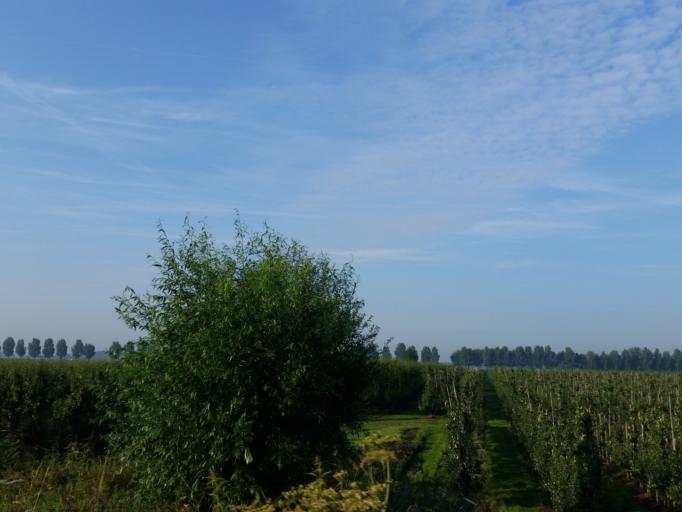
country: NL
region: South Holland
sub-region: Gemeente Leerdam
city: Leerdam
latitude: 51.8716
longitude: 5.1200
